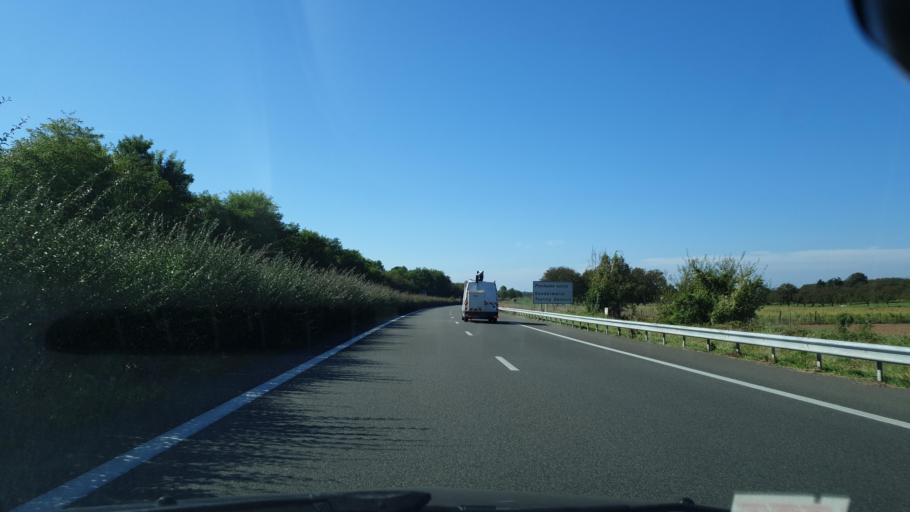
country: FR
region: Rhone-Alpes
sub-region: Departement de l'Isere
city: Saint-Sauveur
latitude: 45.1505
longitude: 5.3548
